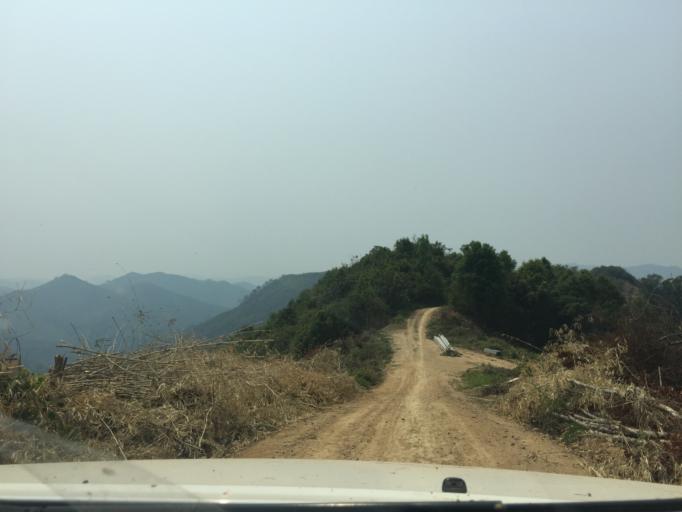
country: LA
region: Loungnamtha
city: Muang Nale
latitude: 20.6290
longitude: 101.6314
